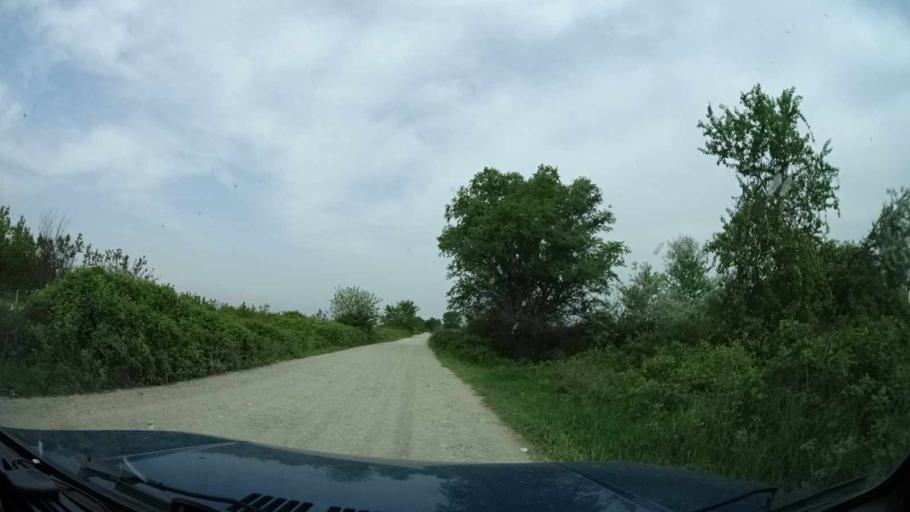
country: AZ
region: Shabran
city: Divichibazar
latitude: 41.3173
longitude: 48.8749
